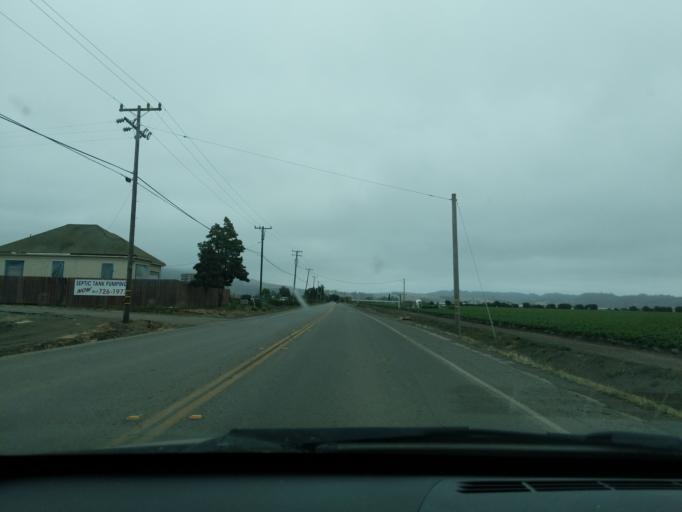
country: US
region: California
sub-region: Monterey County
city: Pajaro
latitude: 36.9040
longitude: -121.7103
